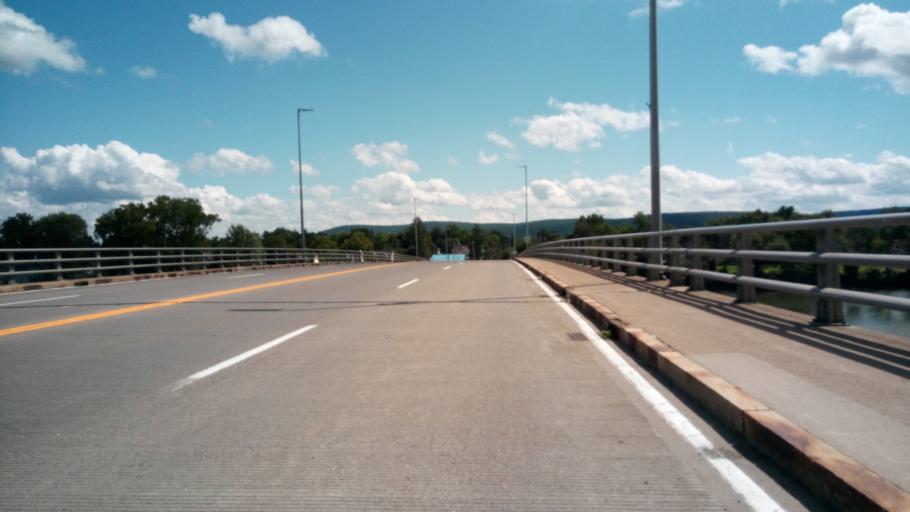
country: US
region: New York
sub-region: Chemung County
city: Elmira
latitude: 42.0838
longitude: -76.8157
